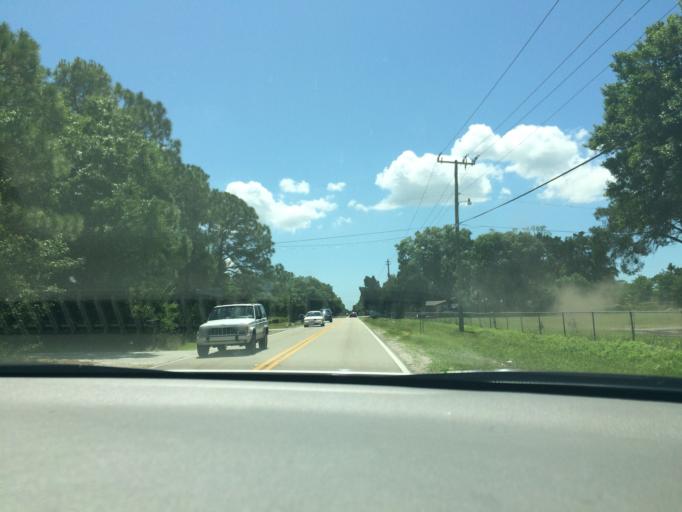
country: US
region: Florida
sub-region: Manatee County
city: Ellenton
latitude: 27.4873
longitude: -82.4896
